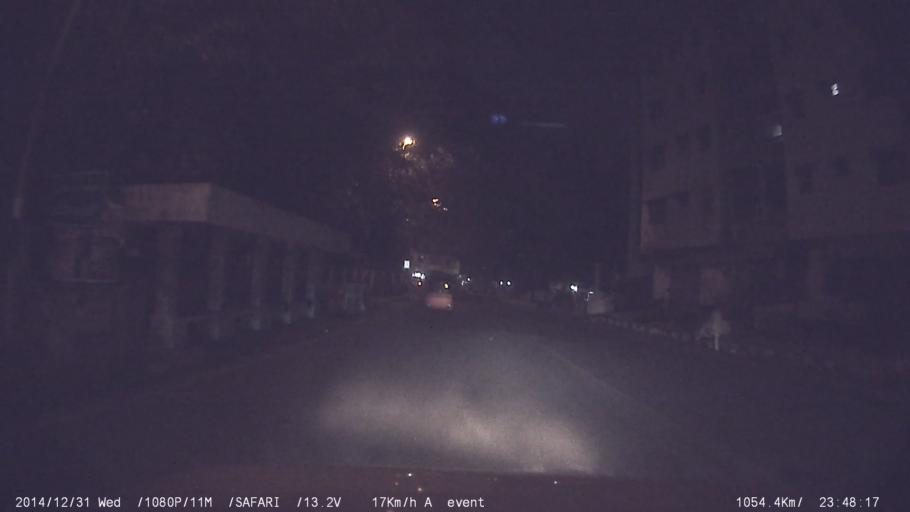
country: IN
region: Tamil Nadu
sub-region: Chennai
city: Chetput
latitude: 13.0817
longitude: 80.2544
